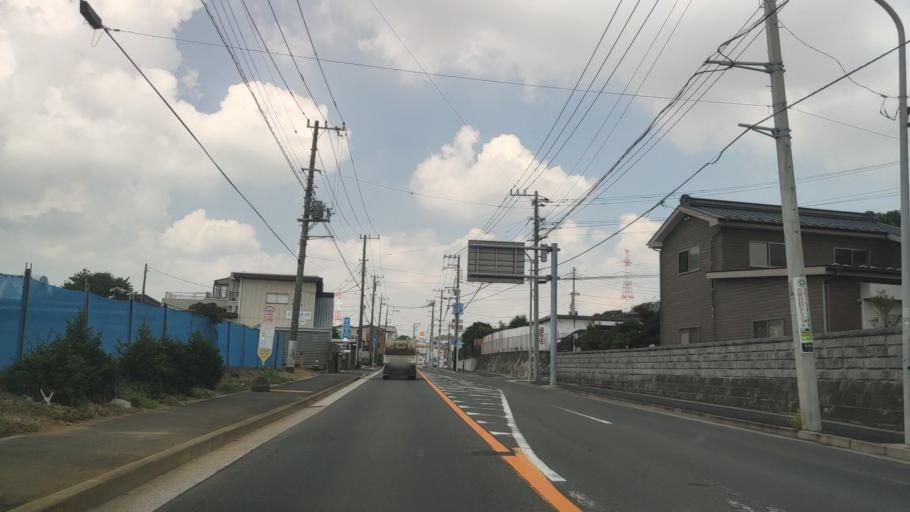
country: JP
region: Kanagawa
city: Minami-rinkan
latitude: 35.4285
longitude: 139.5158
